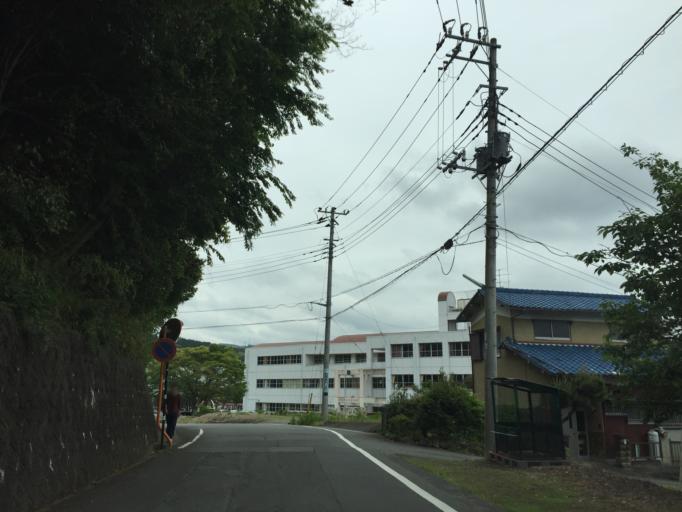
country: JP
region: Shizuoka
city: Mishima
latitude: 35.1745
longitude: 138.9209
